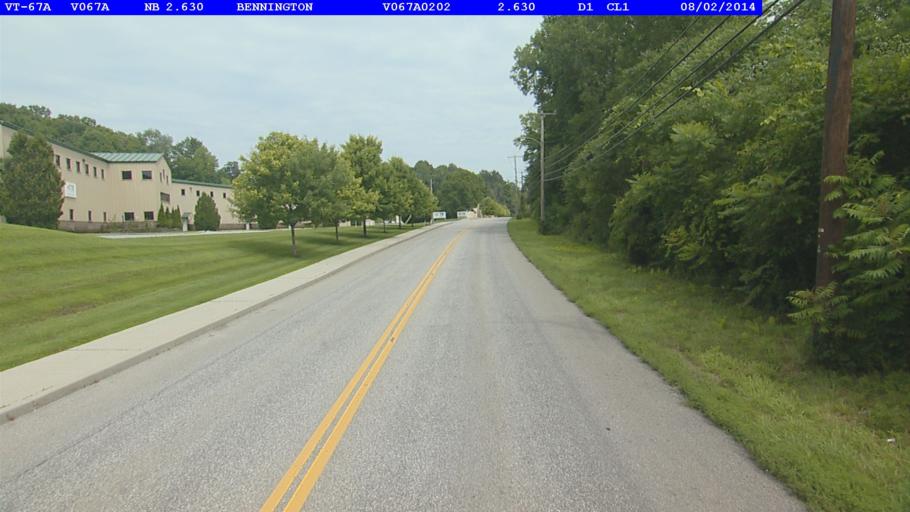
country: US
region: Vermont
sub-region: Bennington County
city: North Bennington
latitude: 42.9205
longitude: -73.2465
